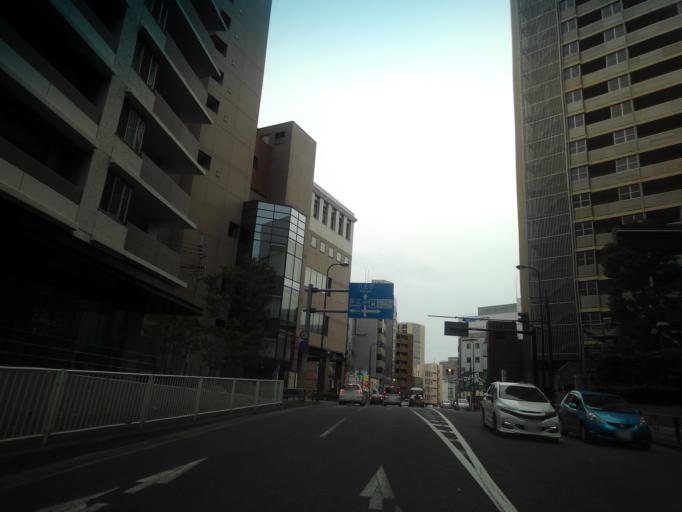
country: JP
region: Tokyo
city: Hino
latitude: 35.6971
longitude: 139.4189
